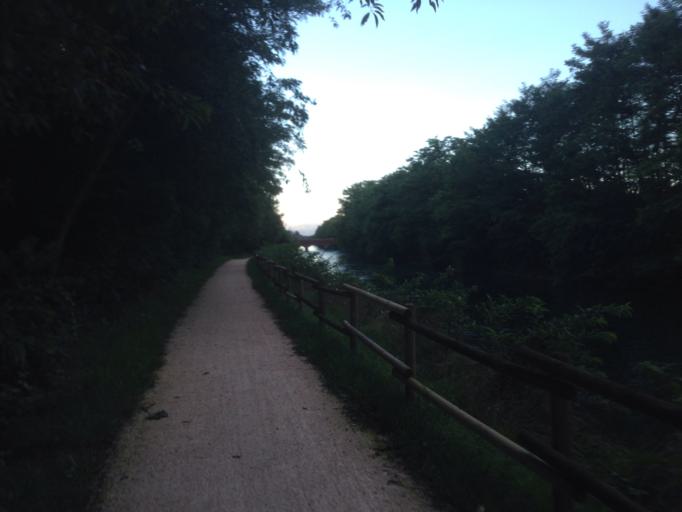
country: IT
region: Lombardy
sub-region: Citta metropolitana di Milano
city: Nosate
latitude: 45.5524
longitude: 8.7388
